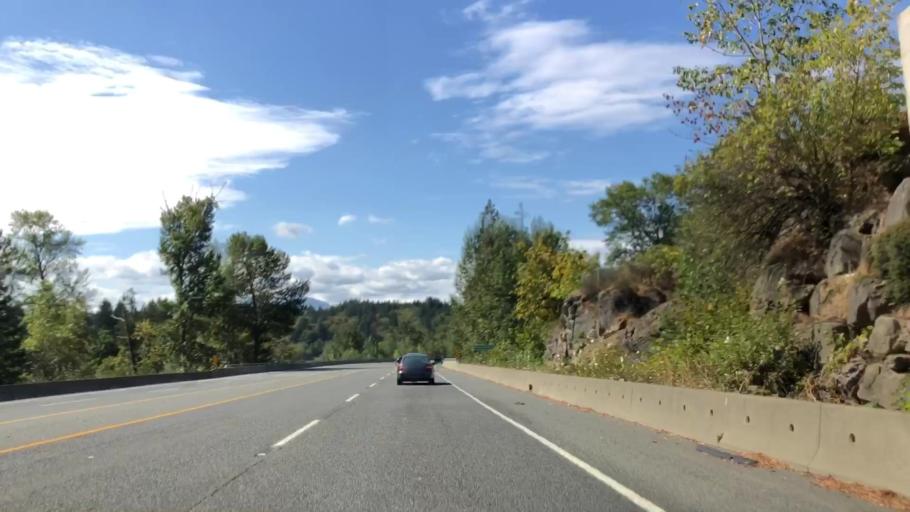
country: CA
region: British Columbia
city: Nanaimo
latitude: 49.1150
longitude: -123.8774
